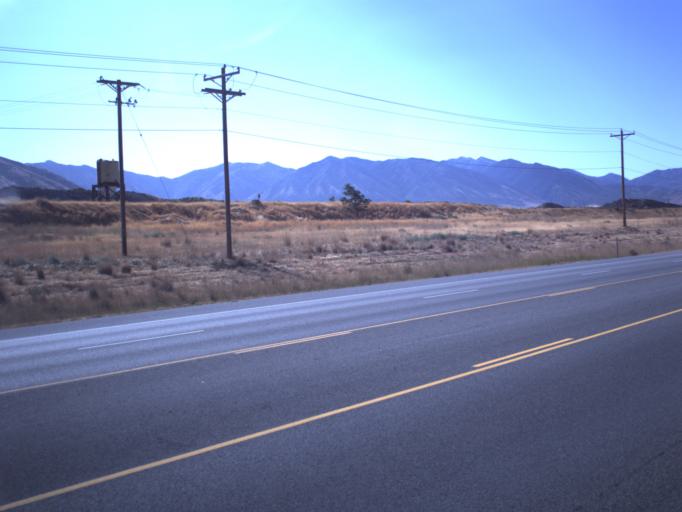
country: US
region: Utah
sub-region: Tooele County
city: Stansbury park
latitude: 40.6354
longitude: -112.2896
